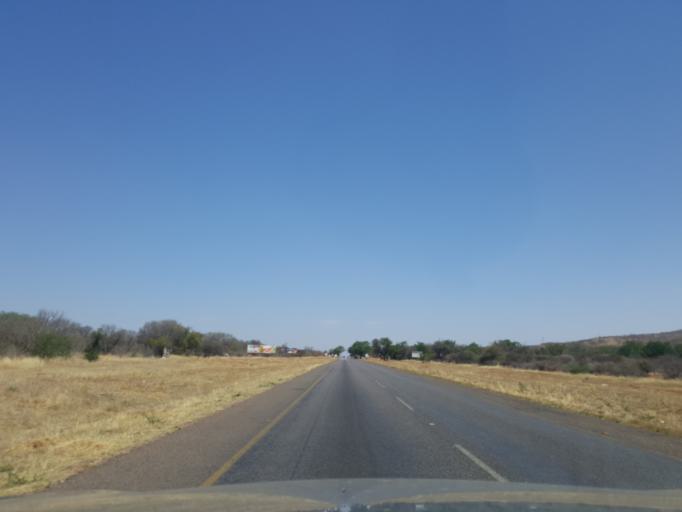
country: BW
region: South East
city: Lobatse
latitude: -25.1664
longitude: 25.6873
